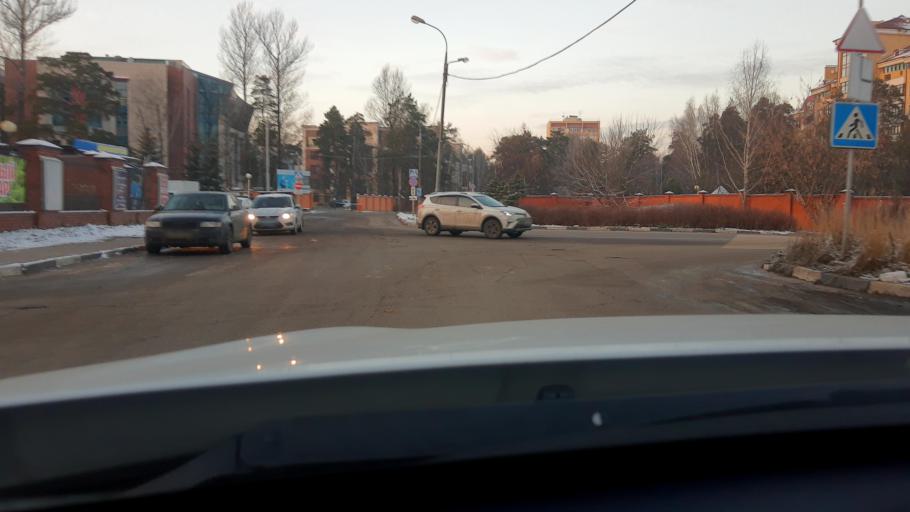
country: RU
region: Moskovskaya
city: Zarech'ye
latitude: 55.6793
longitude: 37.3874
